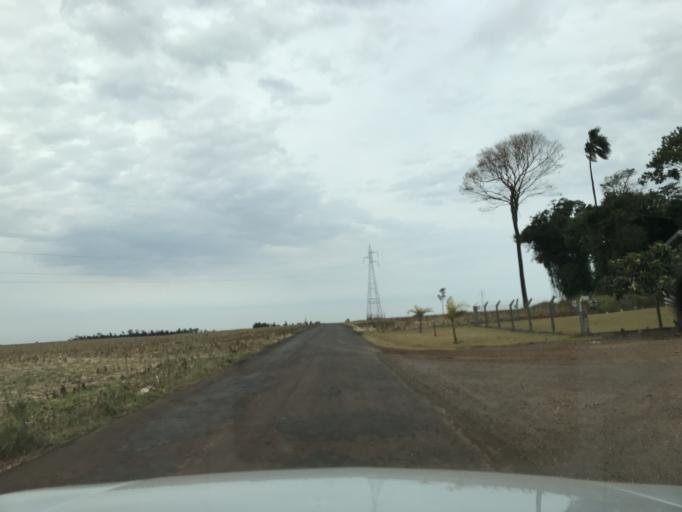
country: BR
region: Parana
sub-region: Palotina
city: Palotina
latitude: -24.2848
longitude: -53.7908
